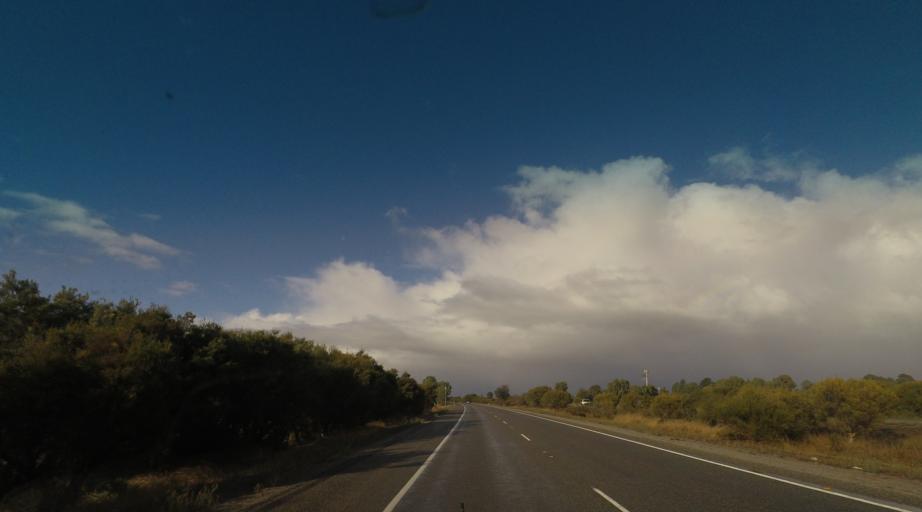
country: AU
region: Western Australia
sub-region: Armadale
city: Seville Grove
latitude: -32.1659
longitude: 115.9613
